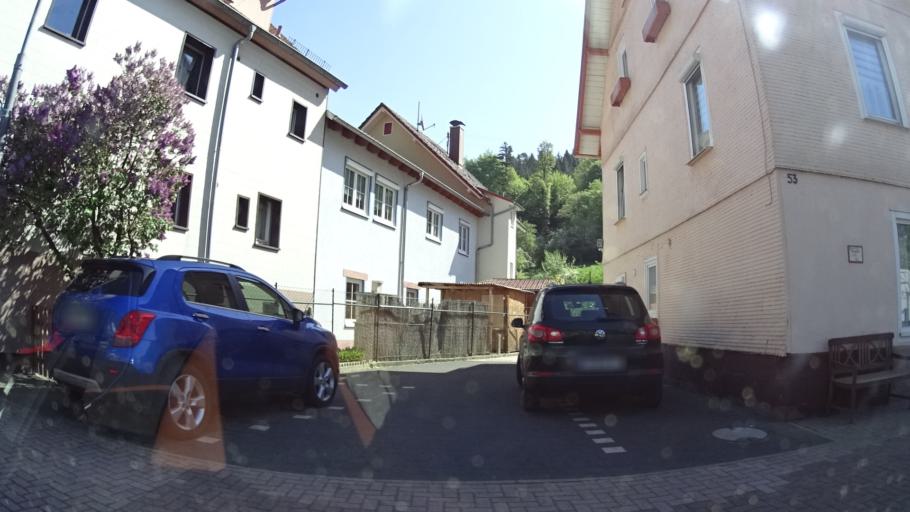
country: DE
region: Baden-Wuerttemberg
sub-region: Karlsruhe Region
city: Hofen an der Enz
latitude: 48.7999
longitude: 8.5833
